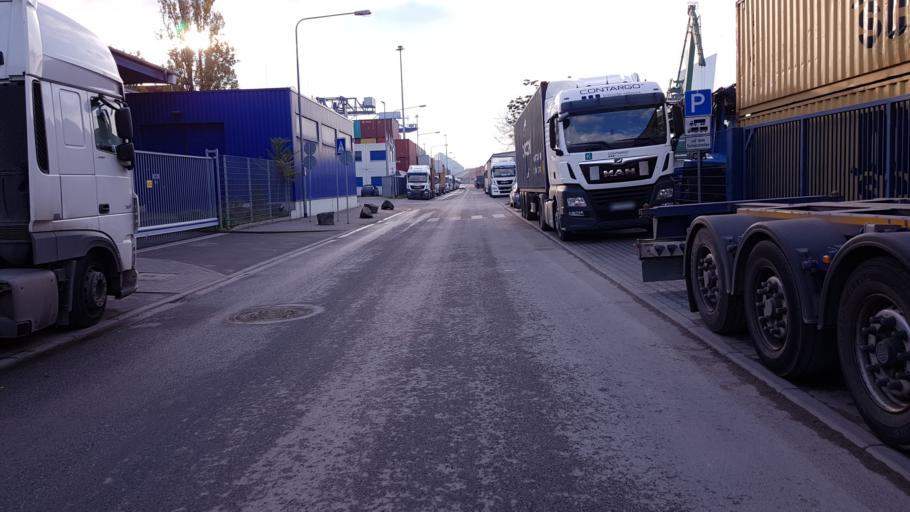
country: DE
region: Hesse
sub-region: Regierungsbezirk Darmstadt
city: Frankfurt am Main
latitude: 50.1108
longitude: 8.7200
